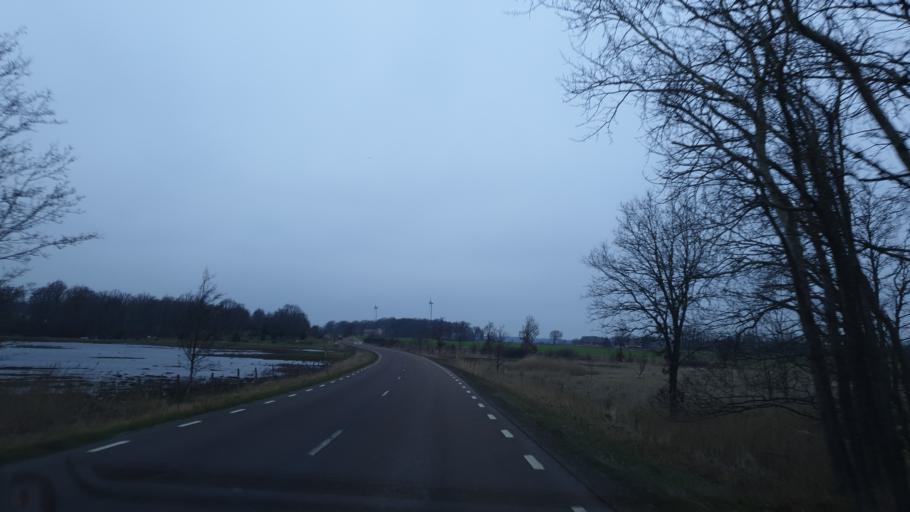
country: SE
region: Blekinge
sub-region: Karlskrona Kommun
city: Jaemjoe
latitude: 56.1606
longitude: 15.7641
